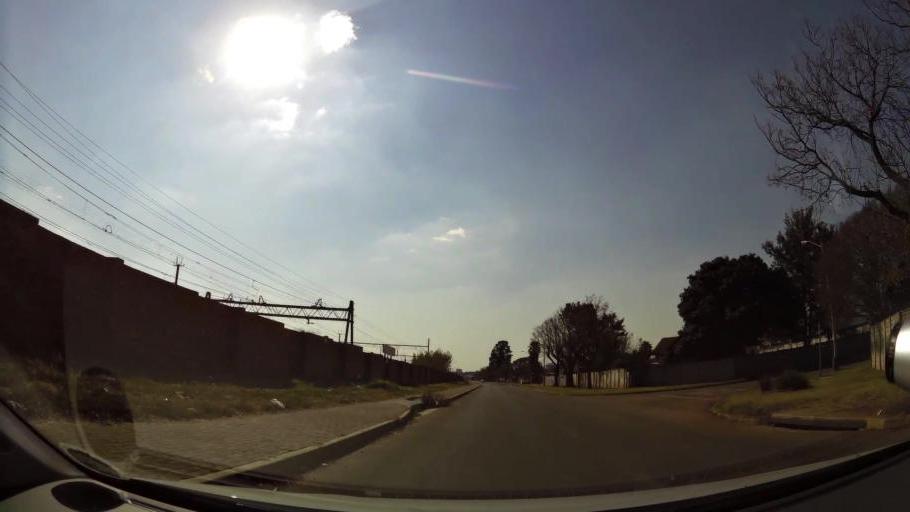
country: ZA
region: Gauteng
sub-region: City of Johannesburg Metropolitan Municipality
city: Modderfontein
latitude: -26.1231
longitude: 28.2262
